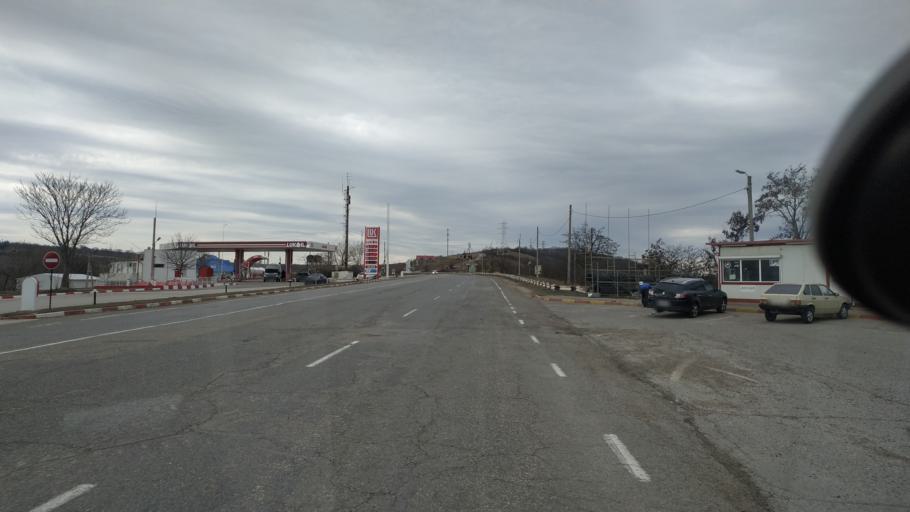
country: MD
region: Chisinau
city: Vadul lui Voda
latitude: 47.0876
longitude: 29.0723
